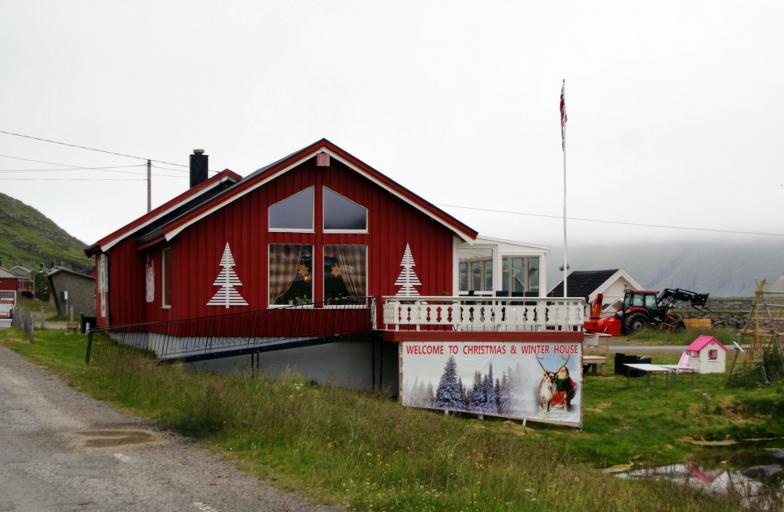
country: NO
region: Finnmark Fylke
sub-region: Nordkapp
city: Honningsvag
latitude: 71.1119
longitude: 25.8217
